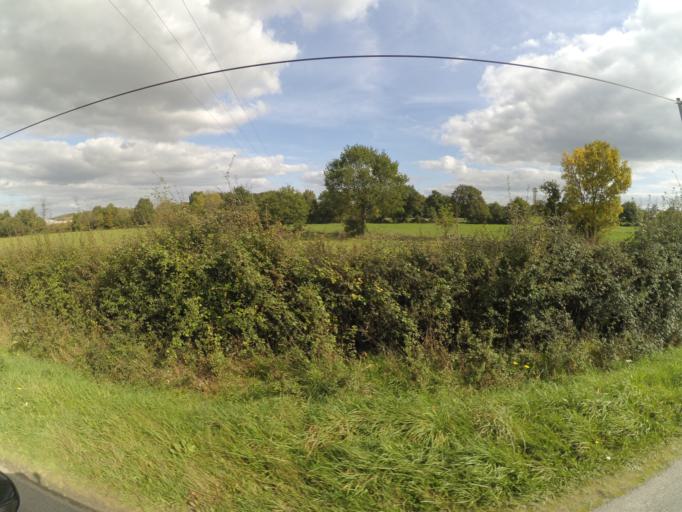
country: FR
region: Pays de la Loire
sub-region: Departement de la Loire-Atlantique
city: Casson
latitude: 47.3913
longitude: -1.5641
